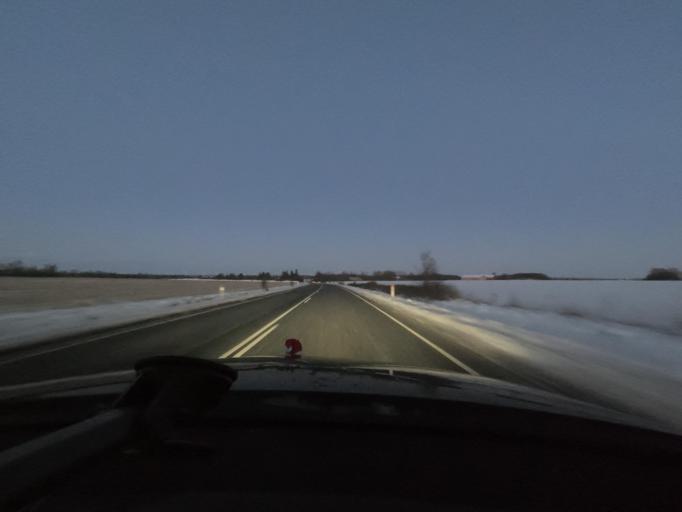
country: DK
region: South Denmark
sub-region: Tonder Kommune
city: Sherrebek
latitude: 55.1729
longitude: 8.7910
